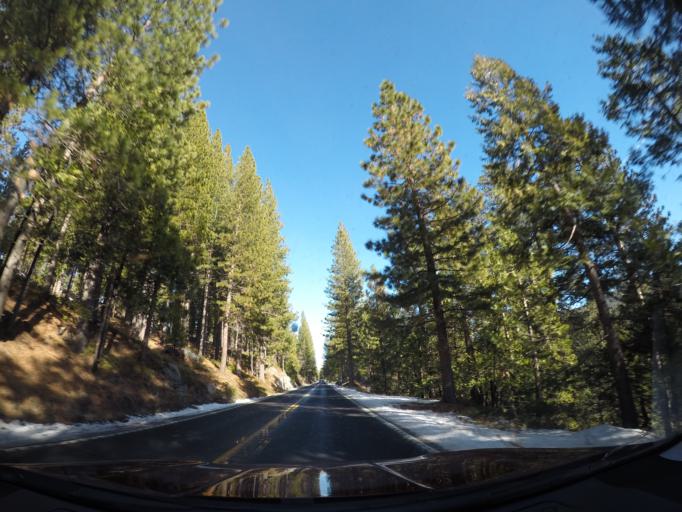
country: US
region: California
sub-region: Tuolumne County
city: Twain Harte
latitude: 38.1759
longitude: -120.0255
